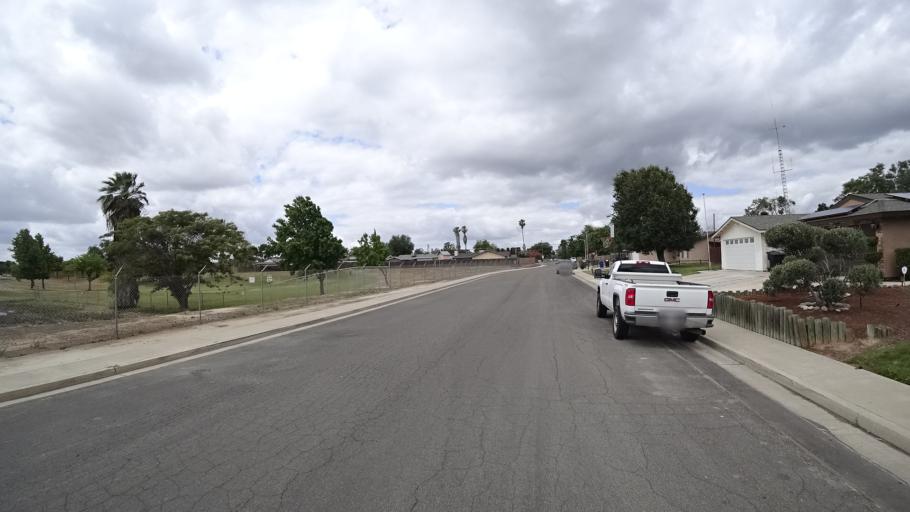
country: US
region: California
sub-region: Kings County
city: Hanford
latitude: 36.3330
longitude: -119.6266
